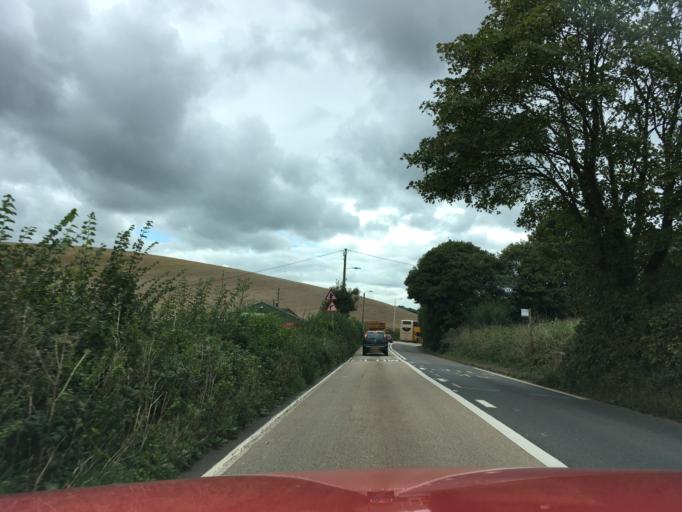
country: GB
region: England
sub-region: Devon
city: Totnes
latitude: 50.4295
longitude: -3.6412
